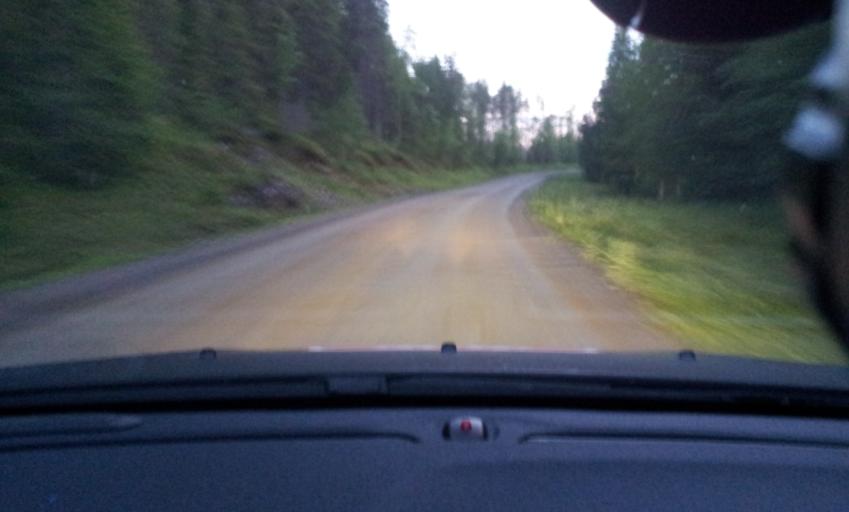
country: SE
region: Vaesternorrland
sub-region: Ange Kommun
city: Ange
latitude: 62.7718
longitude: 15.9257
